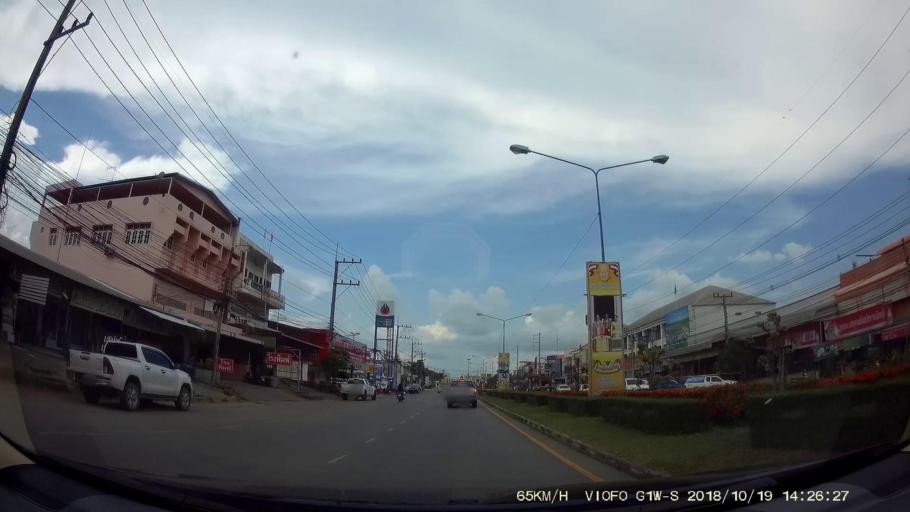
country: TH
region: Chaiyaphum
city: Kaeng Khro
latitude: 16.1064
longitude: 102.2598
